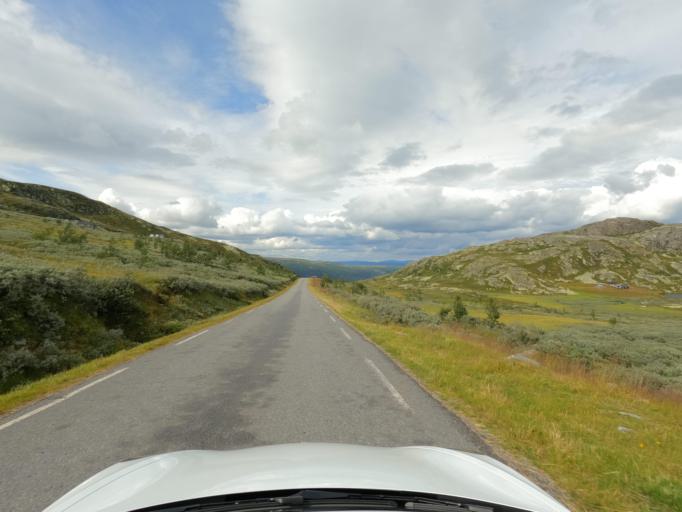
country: NO
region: Telemark
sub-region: Tinn
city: Rjukan
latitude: 59.8509
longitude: 8.6908
